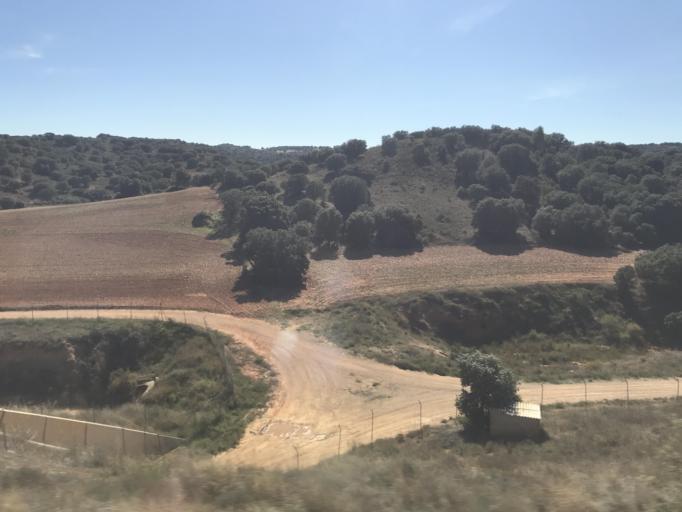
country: ES
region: Aragon
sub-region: Provincia de Zaragoza
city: Cabolafuente
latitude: 41.2409
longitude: -1.9946
